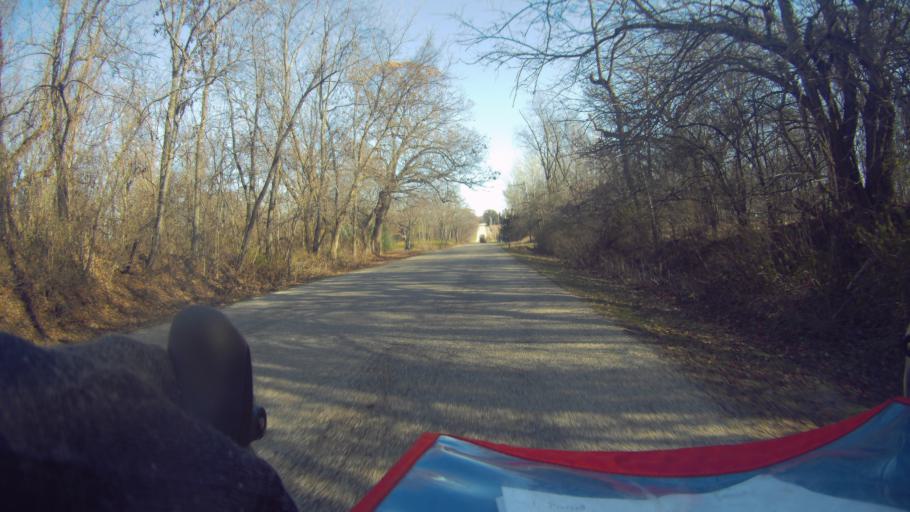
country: US
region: Wisconsin
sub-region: Green County
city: Brooklyn
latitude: 42.8388
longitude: -89.3147
